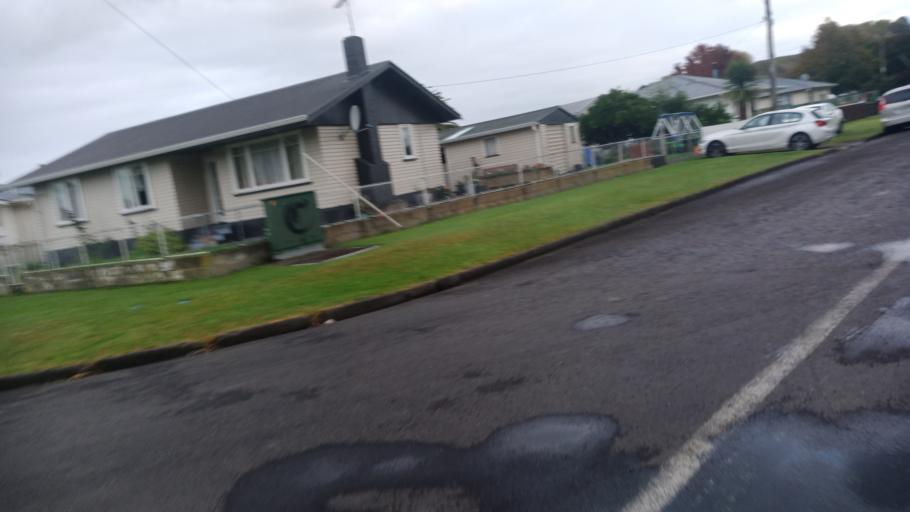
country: NZ
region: Gisborne
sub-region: Gisborne District
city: Gisborne
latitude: -38.6371
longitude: 178.0131
